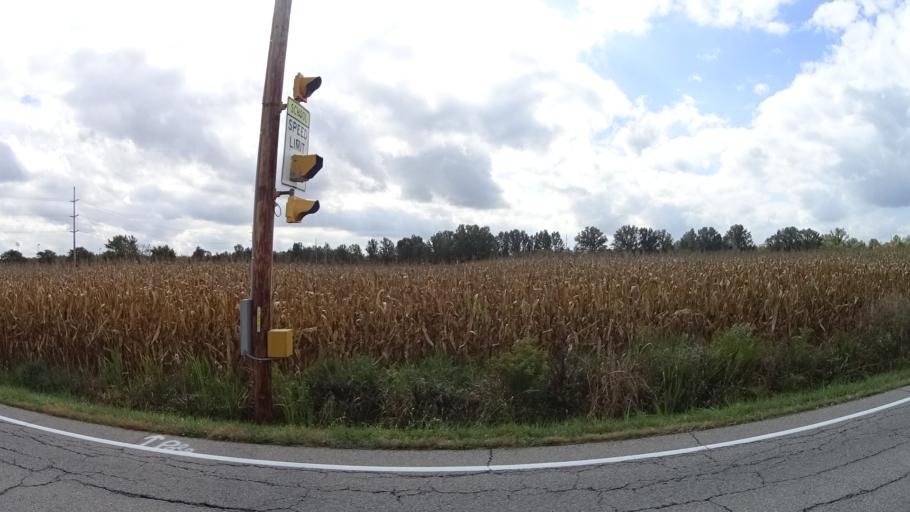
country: US
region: Ohio
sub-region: Lorain County
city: Grafton
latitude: 41.3034
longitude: -82.0658
